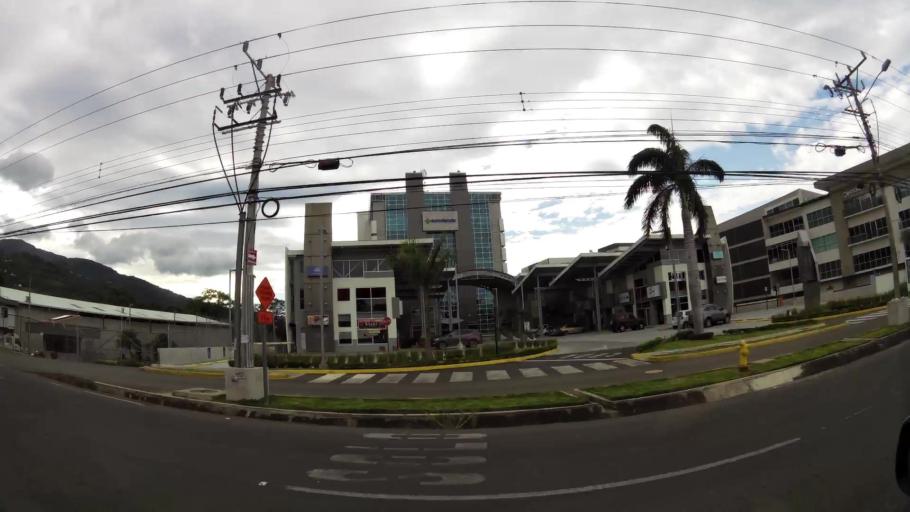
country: CR
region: San Jose
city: Santa Ana
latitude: 9.9351
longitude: -84.1887
